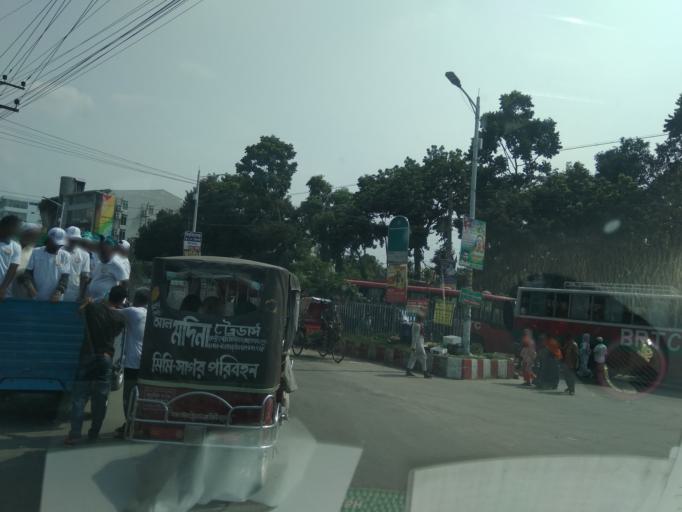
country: BD
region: Rangpur Division
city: Rangpur
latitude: 25.7649
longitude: 89.2315
